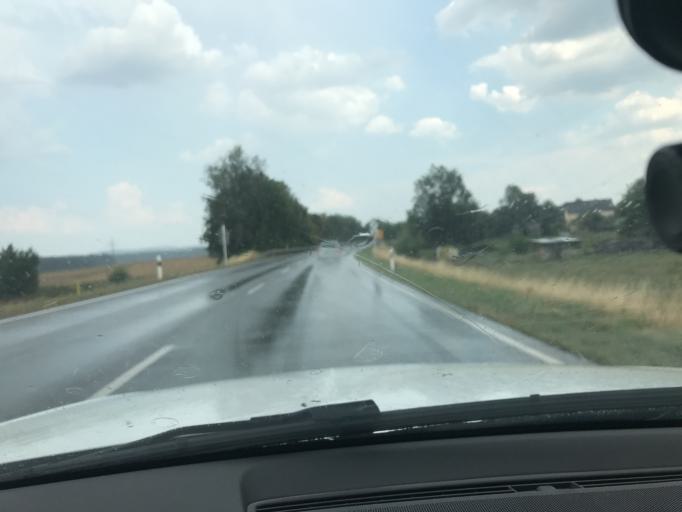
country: DE
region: Bavaria
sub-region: Upper Palatinate
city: Speinshart
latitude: 49.7481
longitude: 11.8507
